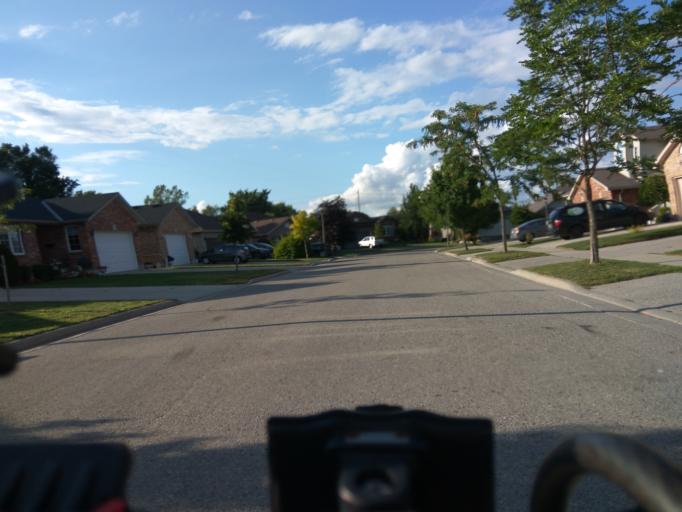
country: CA
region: Ontario
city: Stratford
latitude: 43.3824
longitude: -80.9638
